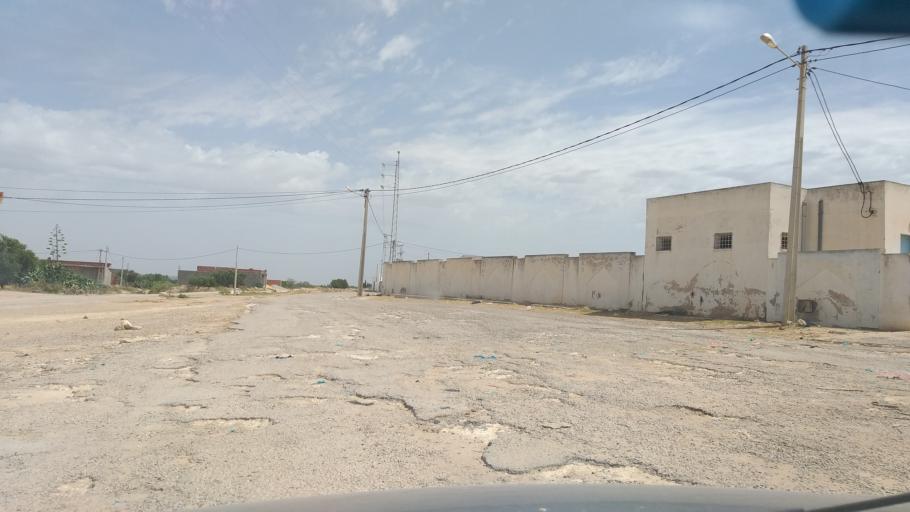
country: TN
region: Al Mahdiyah
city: El Jem
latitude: 35.3116
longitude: 10.7039
